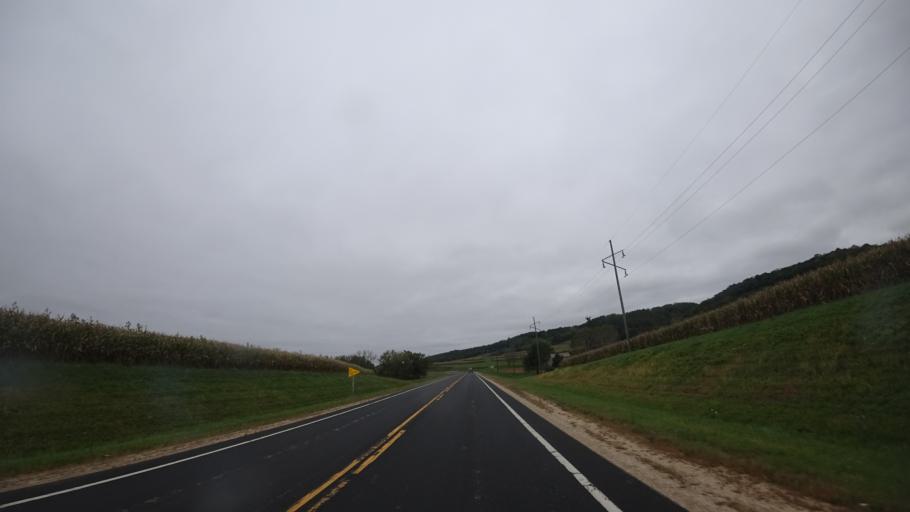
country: US
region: Wisconsin
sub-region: Grant County
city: Boscobel
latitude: 43.1048
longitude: -90.8194
